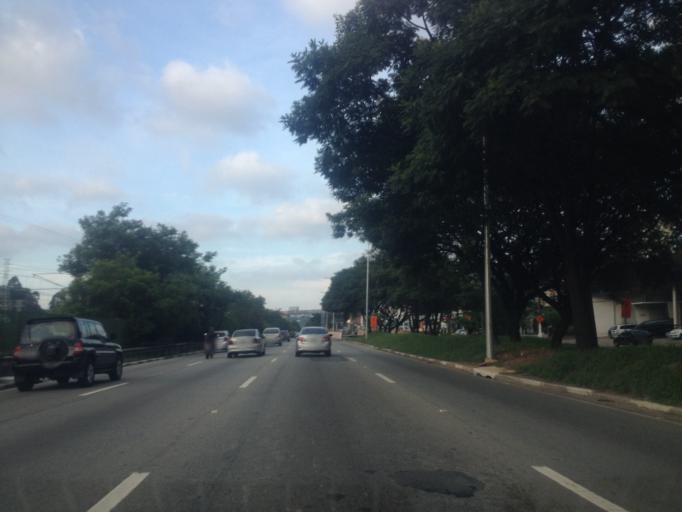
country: BR
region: Sao Paulo
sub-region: Taboao Da Serra
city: Taboao da Serra
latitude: -23.6370
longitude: -46.7204
